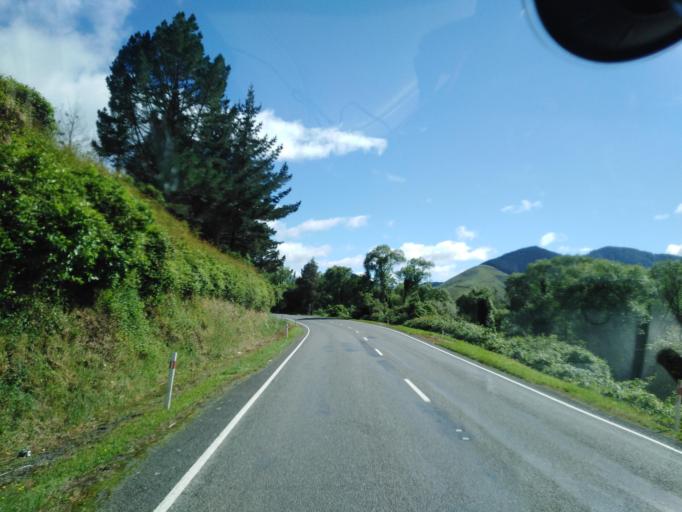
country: NZ
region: Nelson
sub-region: Nelson City
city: Nelson
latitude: -41.2542
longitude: 173.5770
